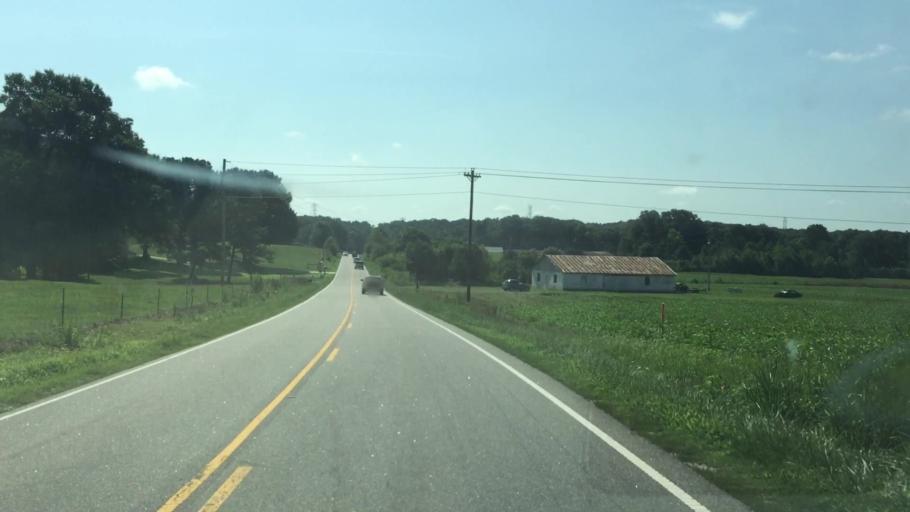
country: US
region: North Carolina
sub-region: Union County
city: Fairview
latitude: 35.1373
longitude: -80.4983
